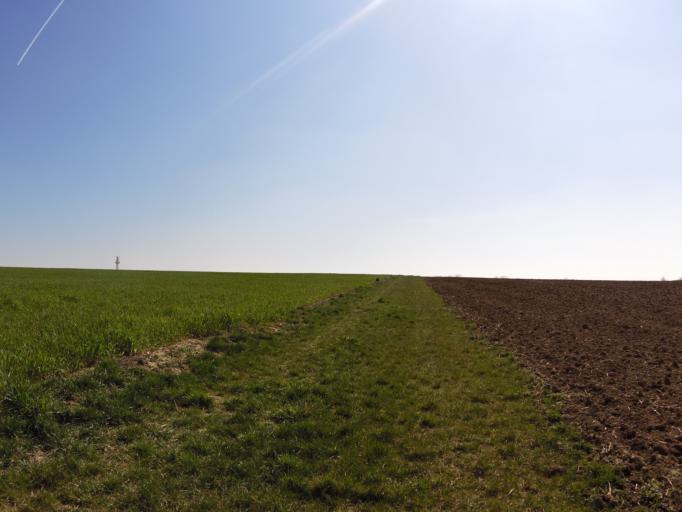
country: DE
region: Bavaria
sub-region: Regierungsbezirk Unterfranken
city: Biebelried
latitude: 49.7422
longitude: 10.0968
